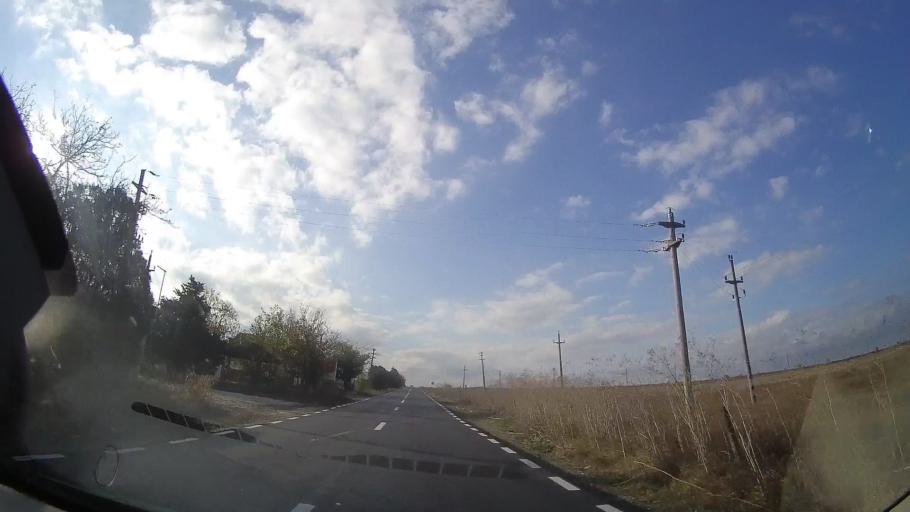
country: RO
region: Constanta
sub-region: Comuna Limanu
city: Limanu
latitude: 43.8237
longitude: 28.5196
